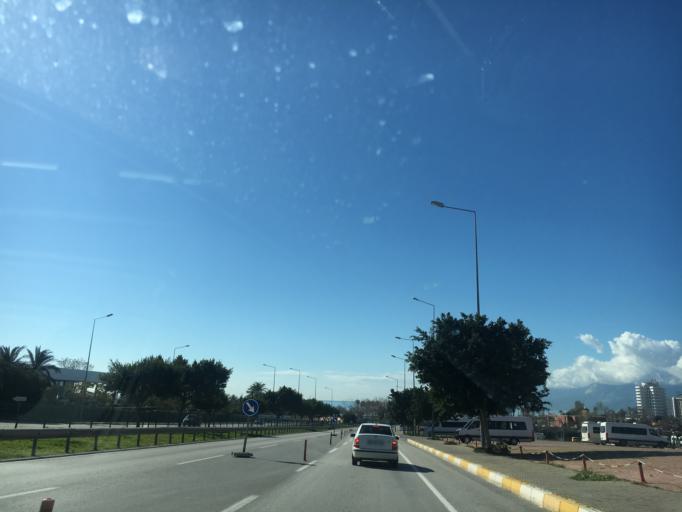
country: TR
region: Antalya
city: Antalya
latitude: 36.8798
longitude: 30.6615
